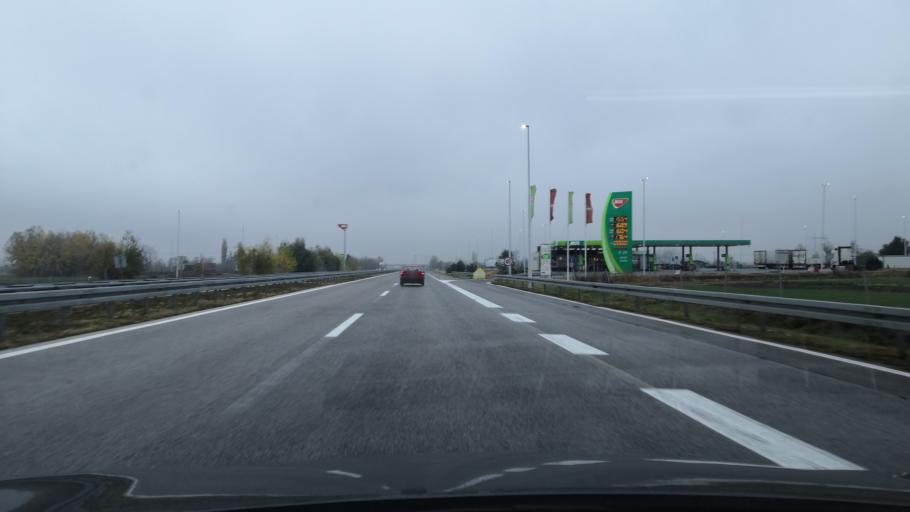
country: HU
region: Csongrad
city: Roszke
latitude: 46.1664
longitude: 19.9611
